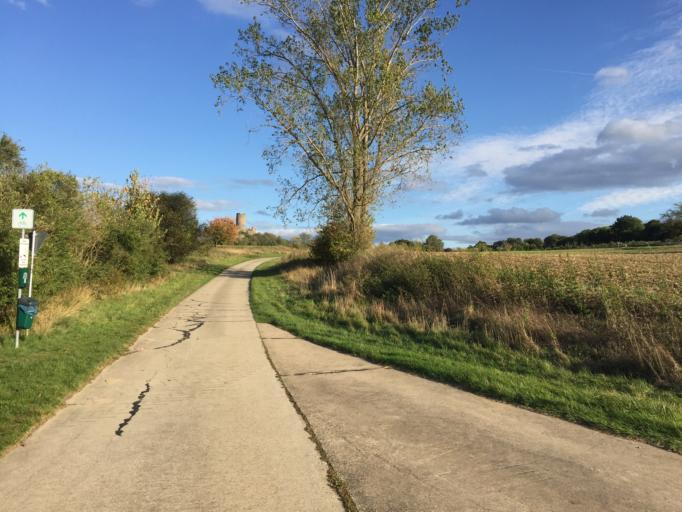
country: DE
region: Hesse
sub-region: Regierungsbezirk Darmstadt
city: Munzenberg
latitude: 50.4534
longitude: 8.7656
